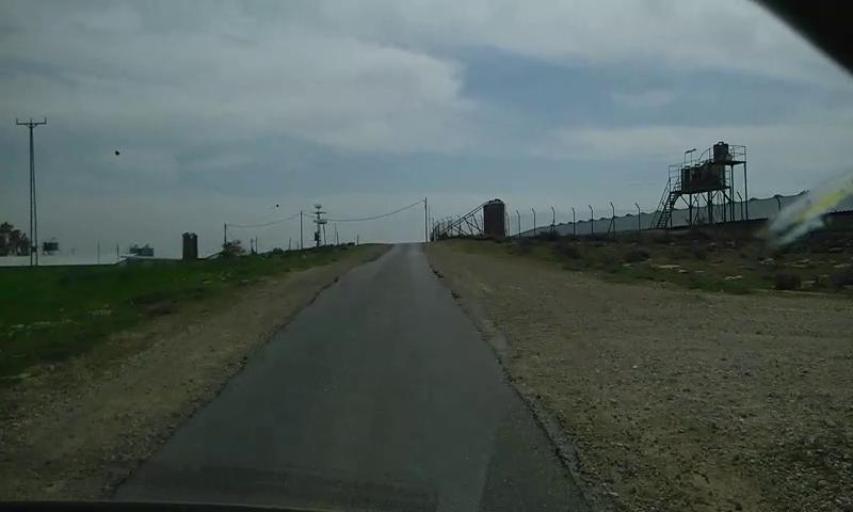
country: PS
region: West Bank
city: Khallat al Mayyah
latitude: 31.4356
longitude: 35.1884
